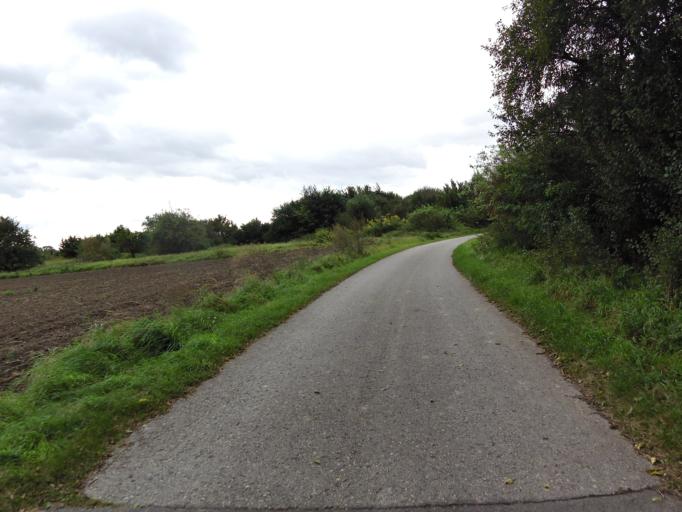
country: DE
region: Saxony-Anhalt
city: Schonhausen
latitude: 52.6007
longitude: 11.9921
